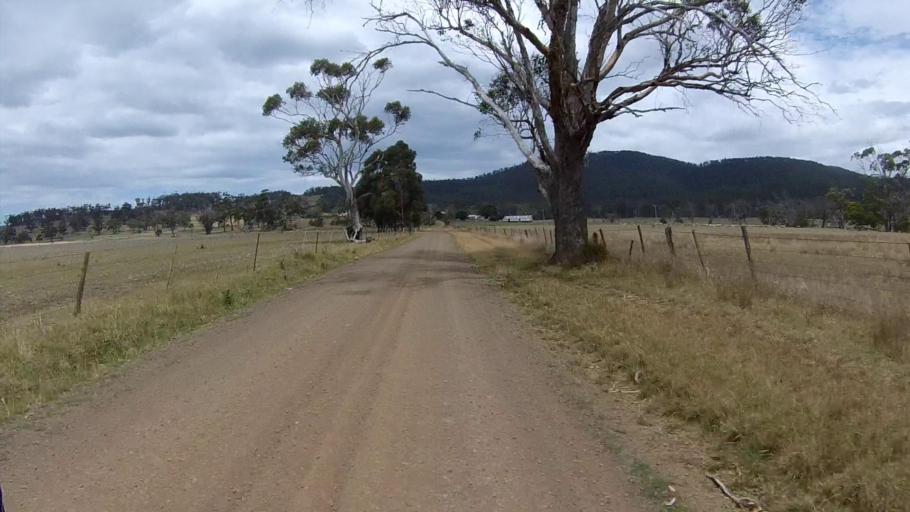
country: AU
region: Tasmania
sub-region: Sorell
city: Sorell
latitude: -42.6569
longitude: 147.9399
